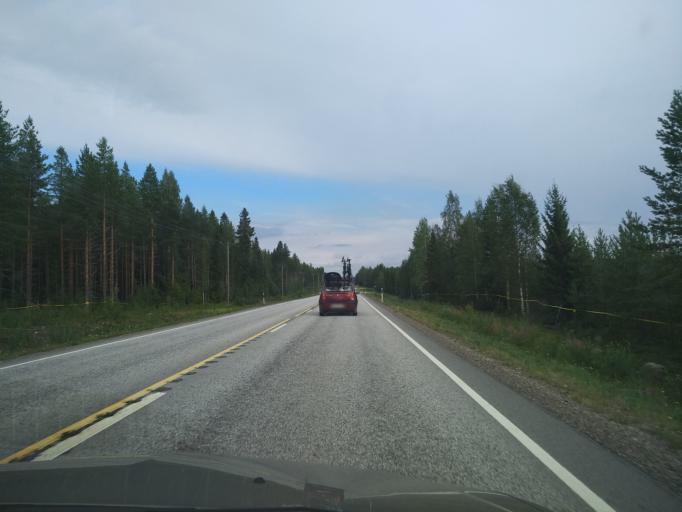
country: FI
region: Kainuu
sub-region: Kajaani
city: Paltamo
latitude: 64.3975
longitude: 27.9144
